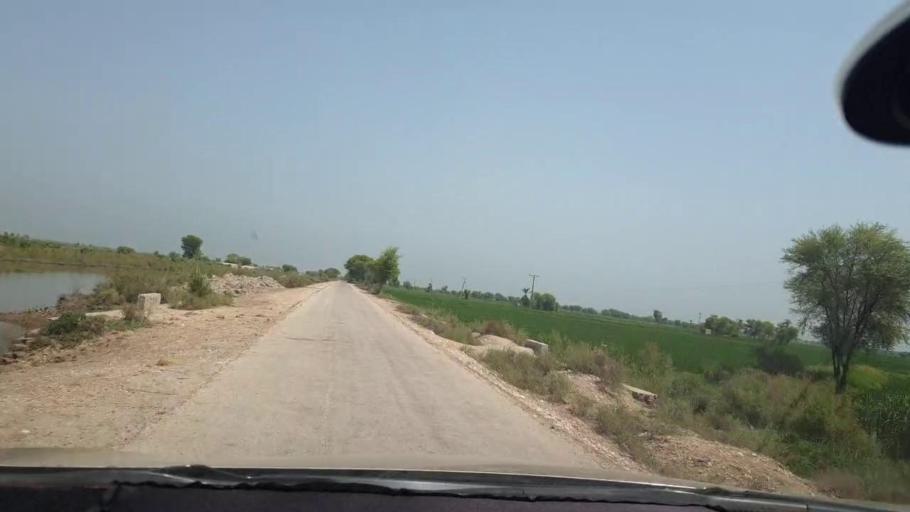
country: PK
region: Sindh
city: Kambar
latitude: 27.6861
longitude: 67.9395
